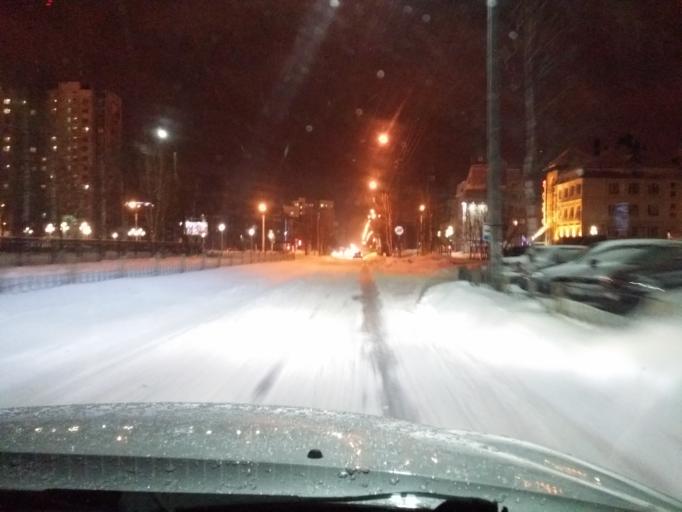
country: RU
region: Khanty-Mansiyskiy Avtonomnyy Okrug
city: Nizhnevartovsk
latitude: 60.9438
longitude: 76.5819
